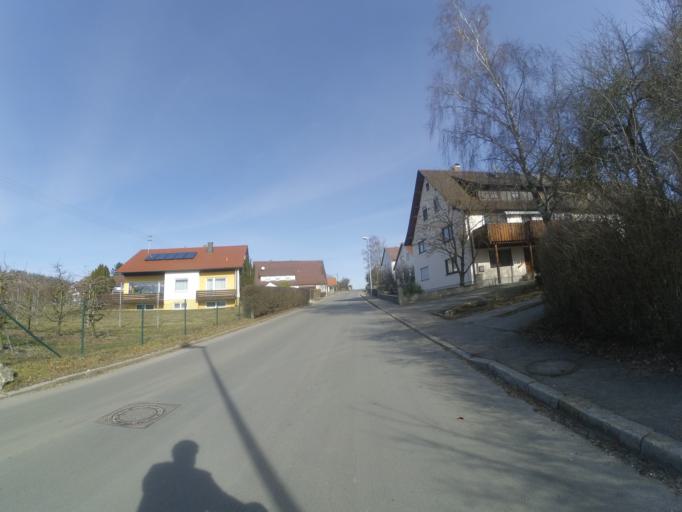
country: DE
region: Baden-Wuerttemberg
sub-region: Tuebingen Region
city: Bernstadt
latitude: 48.4858
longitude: 10.0324
